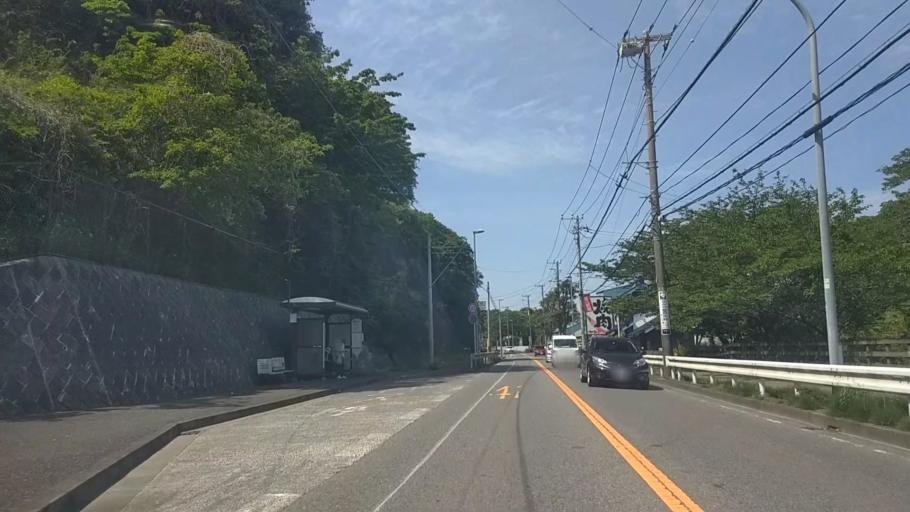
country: JP
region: Kanagawa
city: Kamakura
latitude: 35.3462
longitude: 139.5820
